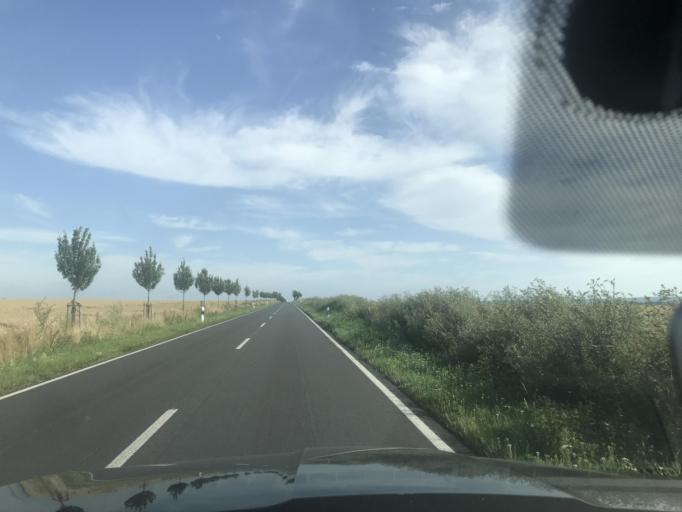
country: DE
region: Saxony-Anhalt
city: Ditfurt
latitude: 51.8582
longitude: 11.1872
